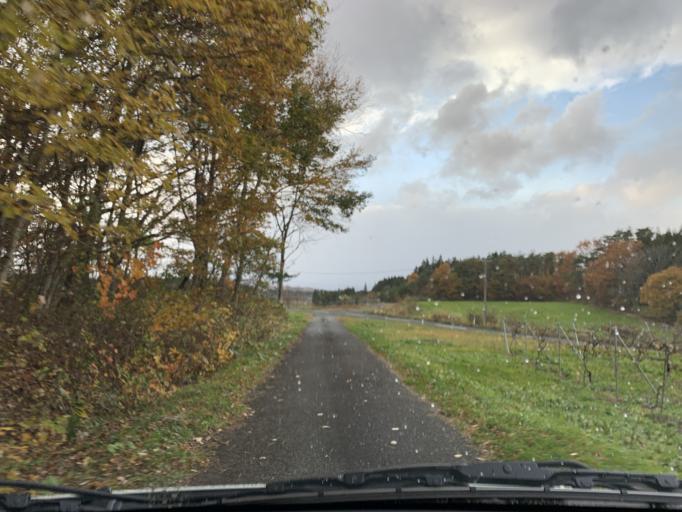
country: JP
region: Iwate
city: Mizusawa
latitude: 39.0883
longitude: 141.0034
